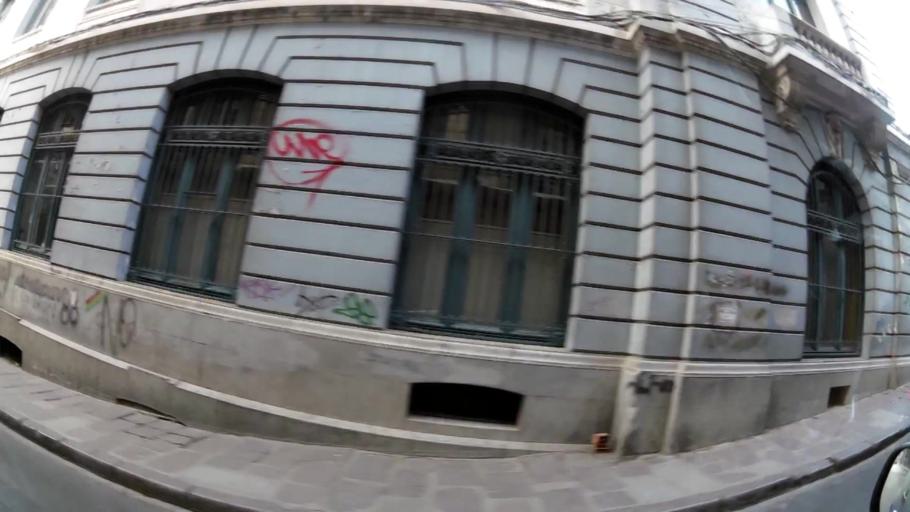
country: BO
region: La Paz
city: La Paz
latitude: -16.4949
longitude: -68.1324
